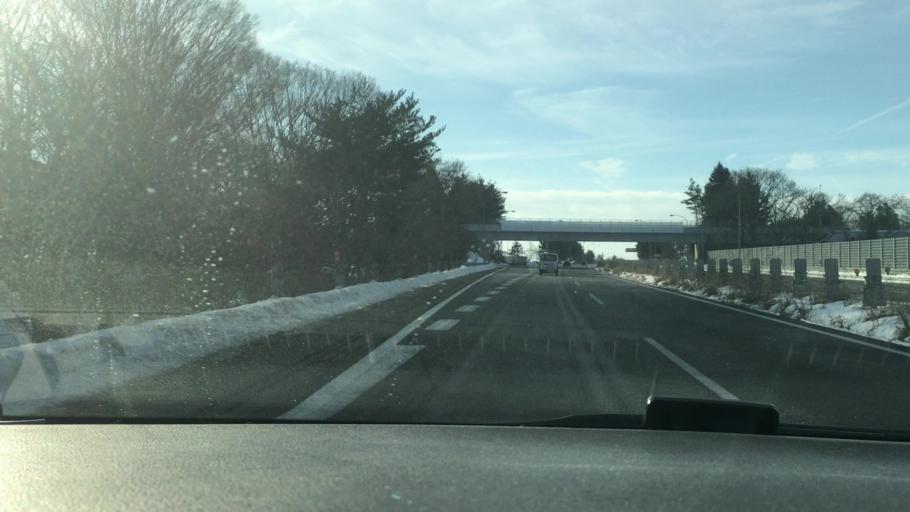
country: JP
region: Iwate
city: Hanamaki
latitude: 39.3724
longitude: 141.0930
